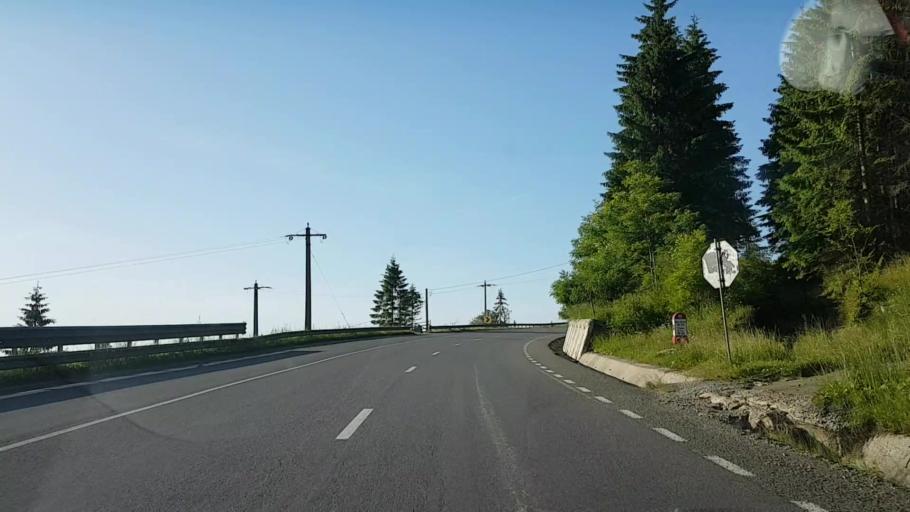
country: RO
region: Bistrita-Nasaud
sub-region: Comuna Lunca Ilvei
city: Lunca Ilvei
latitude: 47.2419
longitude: 25.0191
